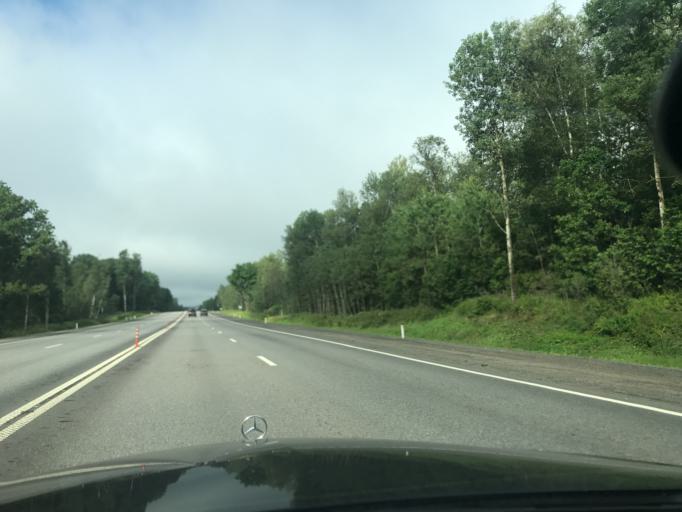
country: RU
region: Smolensk
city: Vyaz'ma
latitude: 55.2768
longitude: 34.4213
